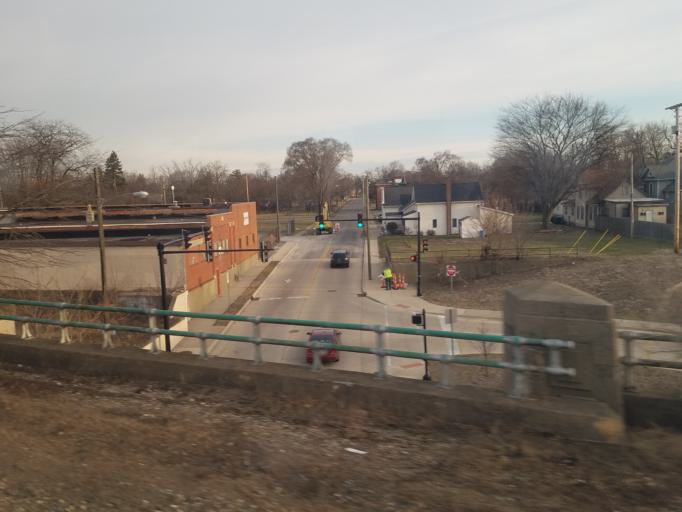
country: US
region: Indiana
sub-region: Saint Joseph County
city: South Bend
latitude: 41.6723
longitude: -86.2702
